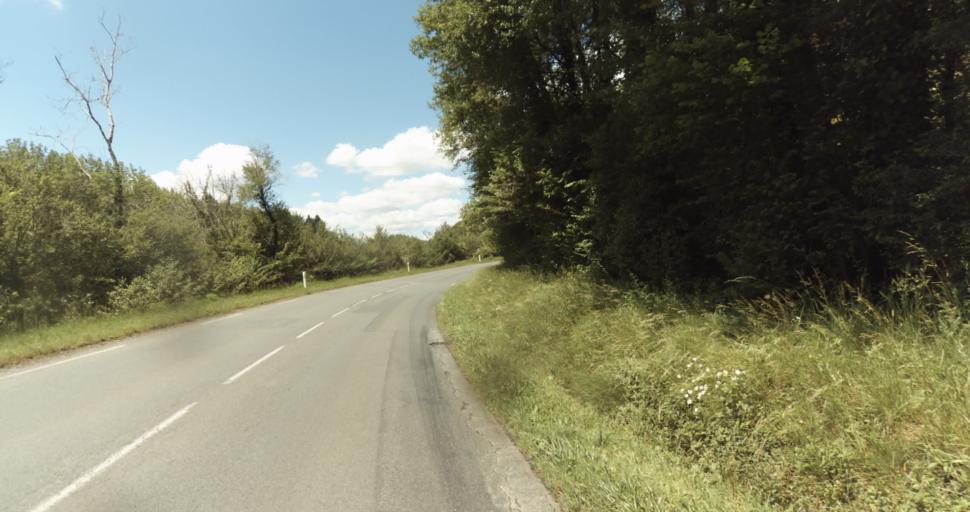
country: FR
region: Aquitaine
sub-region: Departement de la Dordogne
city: Lalinde
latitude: 44.8506
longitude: 0.8112
